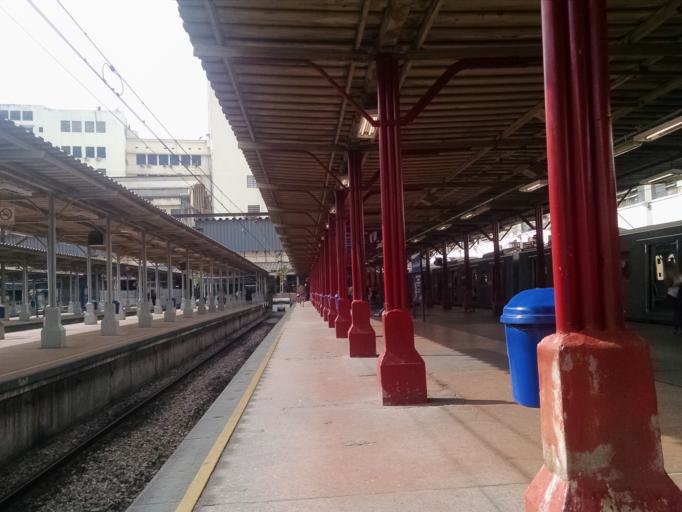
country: BR
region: Rio de Janeiro
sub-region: Rio De Janeiro
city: Rio de Janeiro
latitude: -22.9042
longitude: -43.1926
